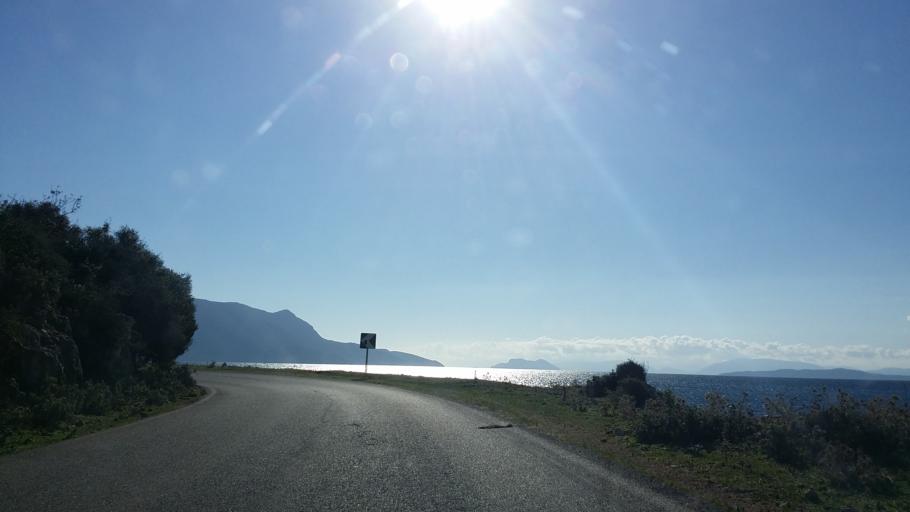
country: GR
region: West Greece
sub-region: Nomos Aitolias kai Akarnanias
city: Kandila
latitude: 38.7074
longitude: 20.8951
